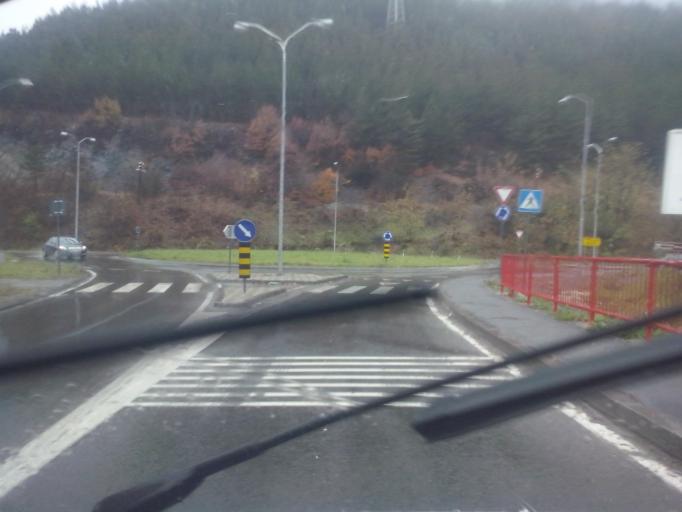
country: RS
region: Central Serbia
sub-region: Raski Okrug
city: Raska
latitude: 43.2870
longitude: 20.6204
